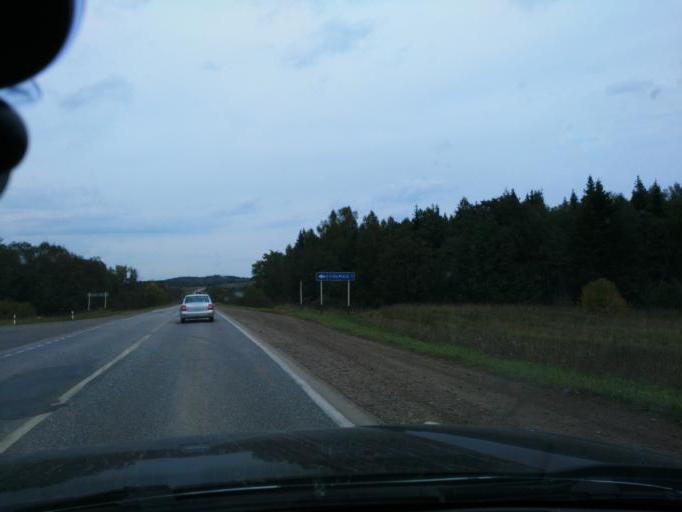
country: RU
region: Perm
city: Chernushka
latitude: 56.5572
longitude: 56.1123
